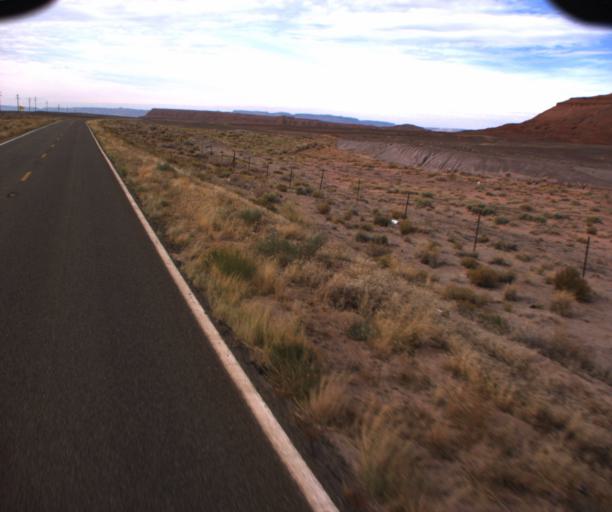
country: US
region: Arizona
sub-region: Apache County
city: Many Farms
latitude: 36.4730
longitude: -109.5196
